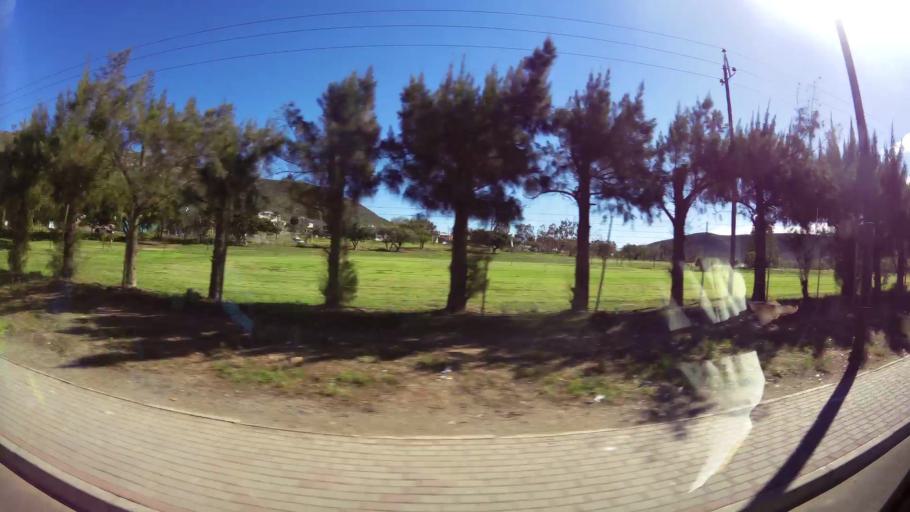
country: ZA
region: Western Cape
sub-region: Cape Winelands District Municipality
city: Ashton
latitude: -33.7755
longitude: 20.1330
